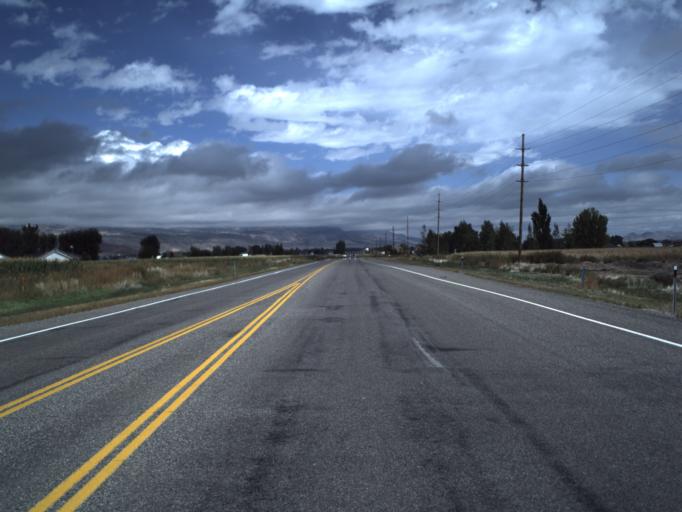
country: US
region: Utah
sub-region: Sevier County
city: Richfield
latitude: 38.7054
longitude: -112.1090
